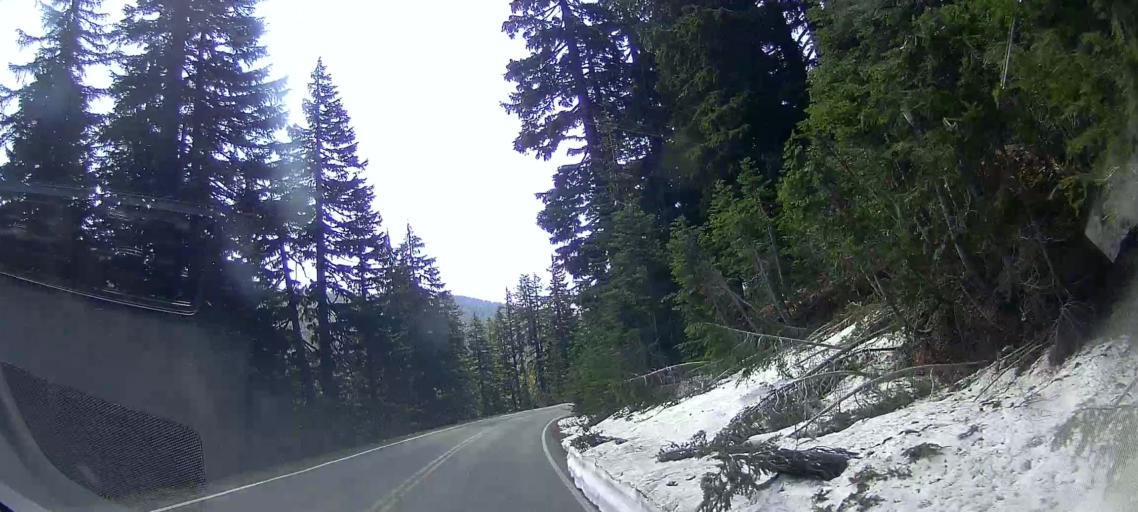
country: US
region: Oregon
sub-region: Klamath County
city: Klamath Falls
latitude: 42.8917
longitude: -122.0971
